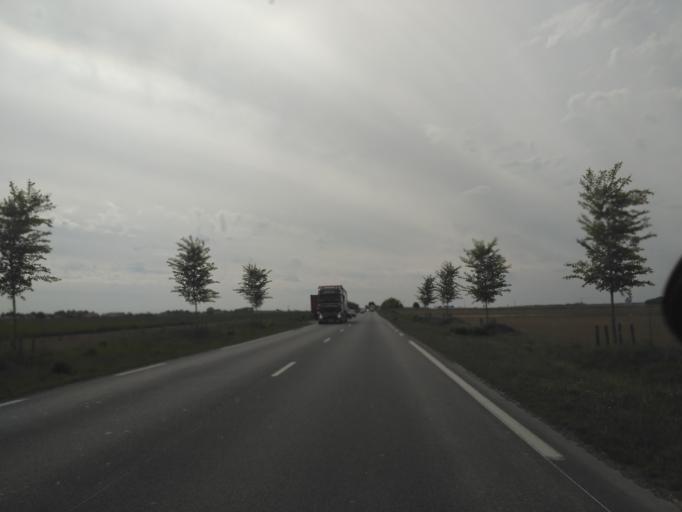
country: FR
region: Ile-de-France
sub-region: Departement de Seine-et-Marne
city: Soignolles-en-Brie
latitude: 48.6333
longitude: 2.7103
